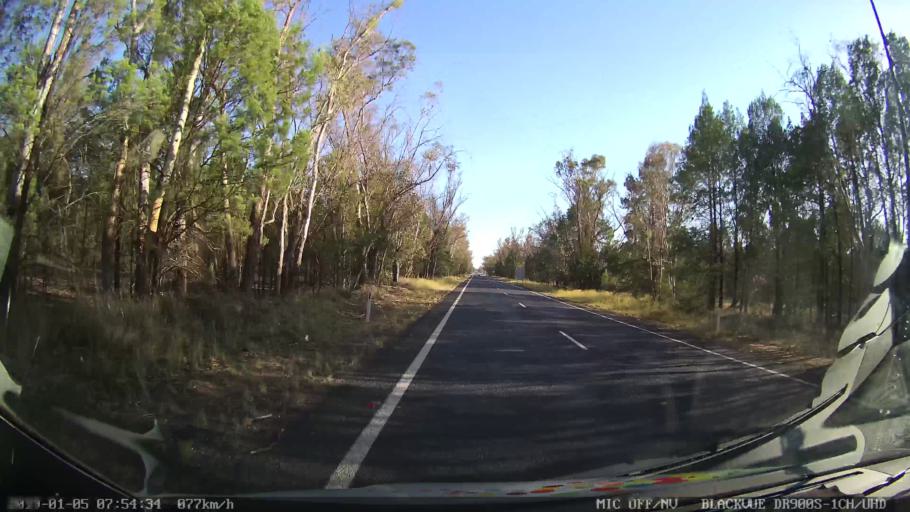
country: AU
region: New South Wales
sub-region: Gilgandra
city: Gilgandra
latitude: -31.7319
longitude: 148.6499
